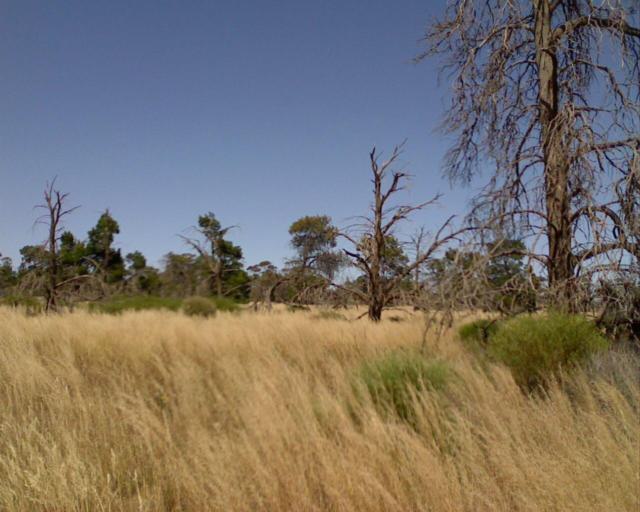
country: AU
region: South Australia
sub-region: Kimba
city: Caralue
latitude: -33.1589
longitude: 135.8749
